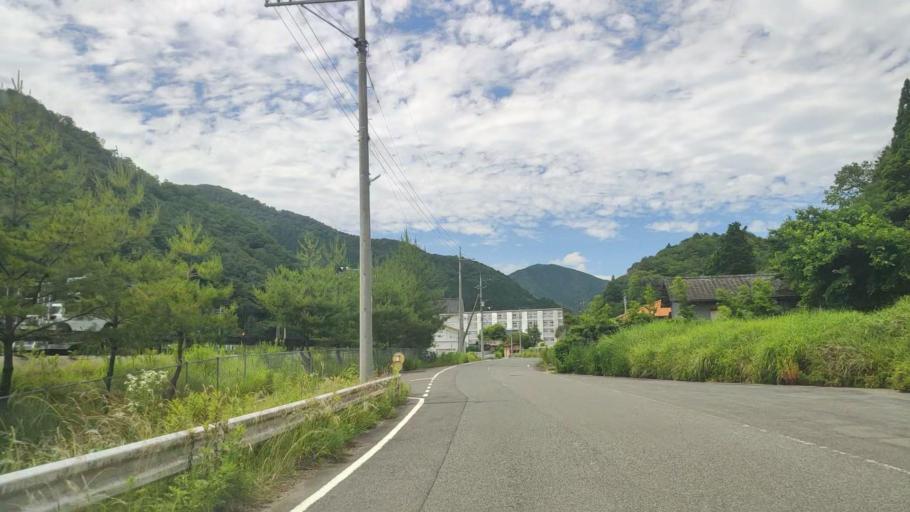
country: JP
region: Hyogo
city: Yamazakicho-nakabirose
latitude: 35.1078
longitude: 134.3285
